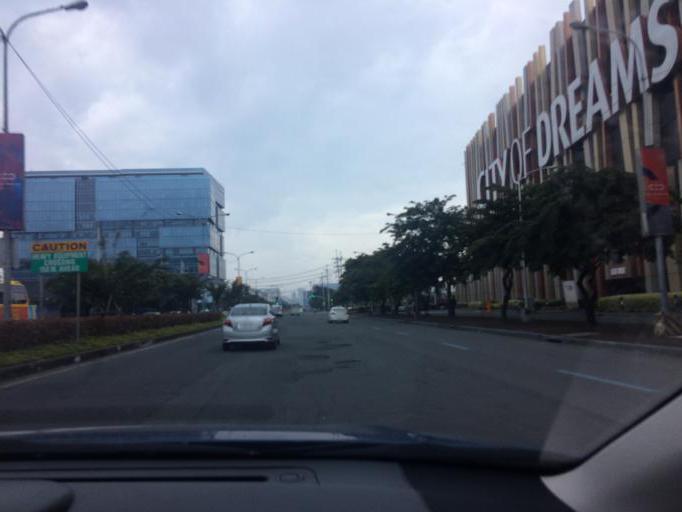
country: PH
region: Metro Manila
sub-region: Makati City
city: Makati City
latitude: 14.5234
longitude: 120.9906
